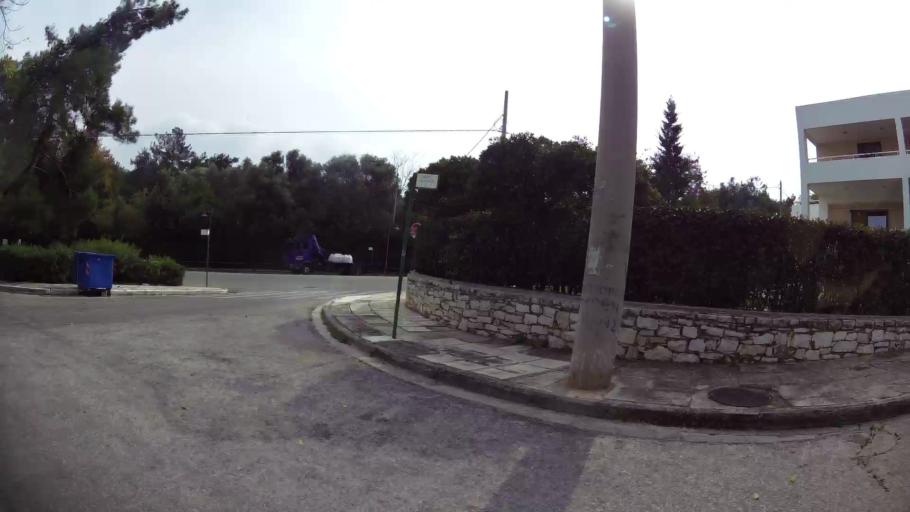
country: GR
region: Attica
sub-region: Nomarchia Athinas
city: Filothei
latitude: 38.0236
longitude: 23.7780
